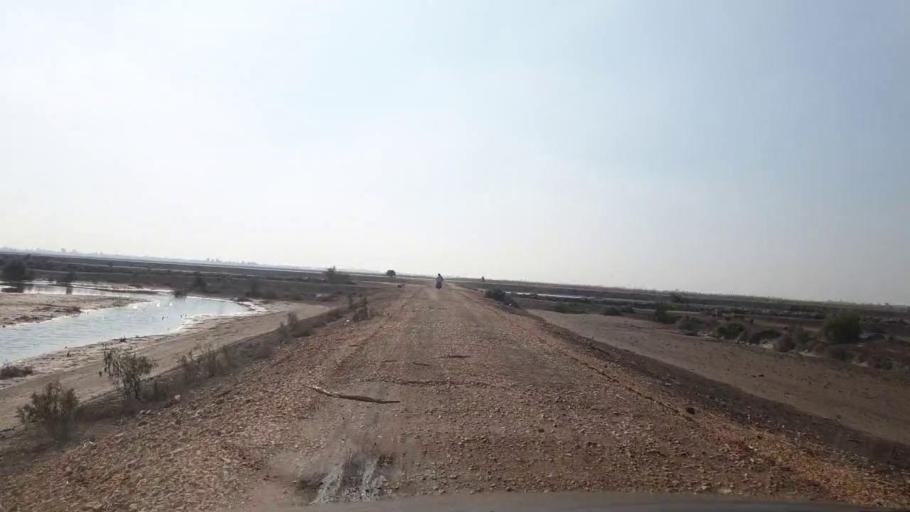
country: PK
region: Sindh
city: Sinjhoro
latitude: 26.0324
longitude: 68.7789
